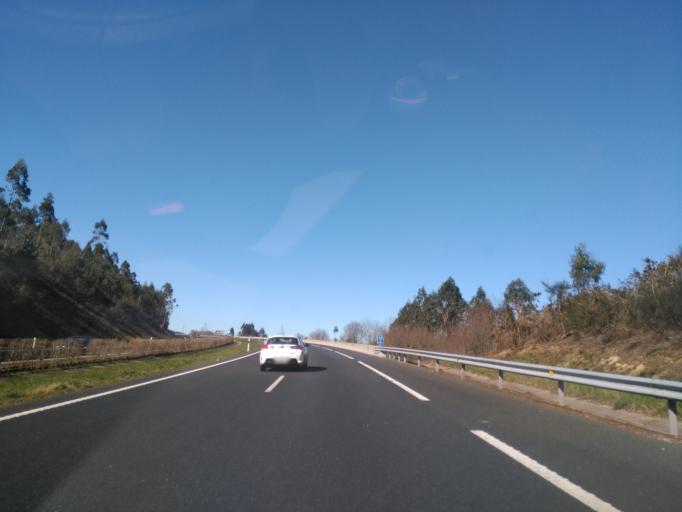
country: ES
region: Cantabria
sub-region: Provincia de Cantabria
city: Cabezon de la Sal
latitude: 43.3206
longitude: -4.2700
